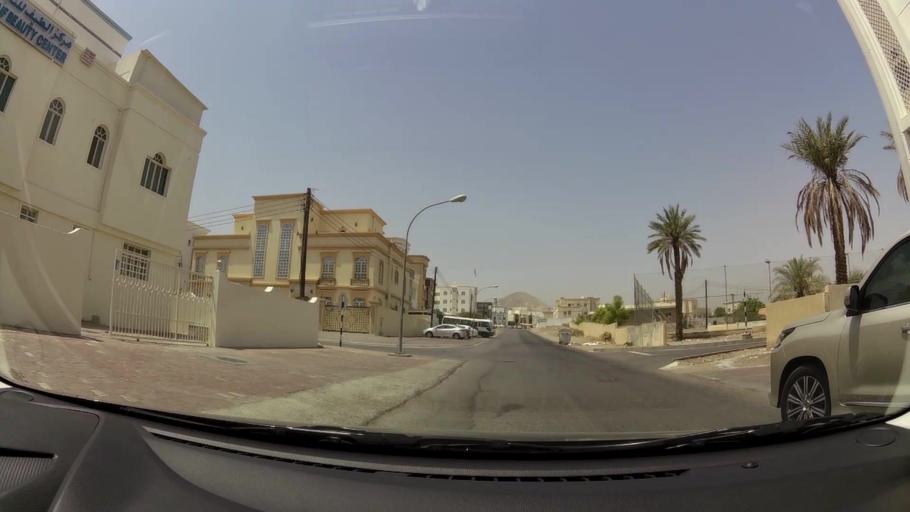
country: OM
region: Muhafazat Masqat
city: Bawshar
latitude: 23.5885
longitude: 58.4424
